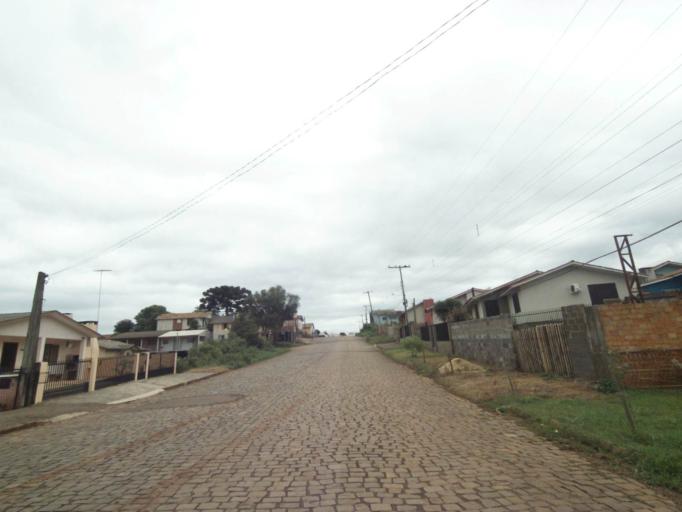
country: BR
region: Rio Grande do Sul
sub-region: Lagoa Vermelha
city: Lagoa Vermelha
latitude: -28.2176
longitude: -51.5359
